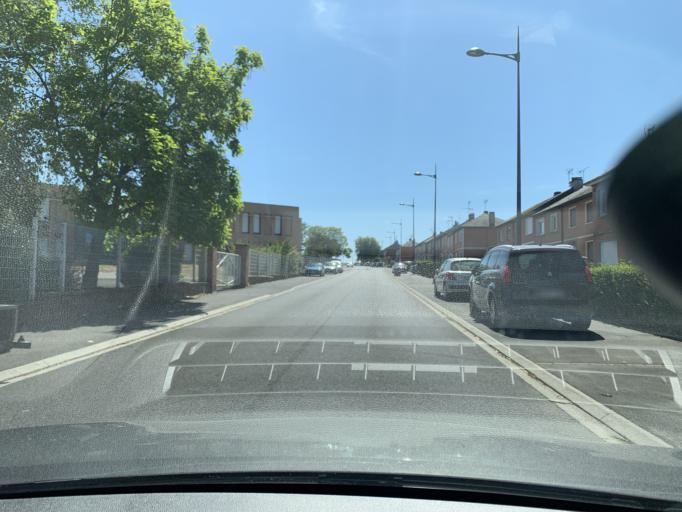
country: FR
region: Nord-Pas-de-Calais
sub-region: Departement du Nord
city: Cambrai
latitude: 50.1604
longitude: 3.2605
